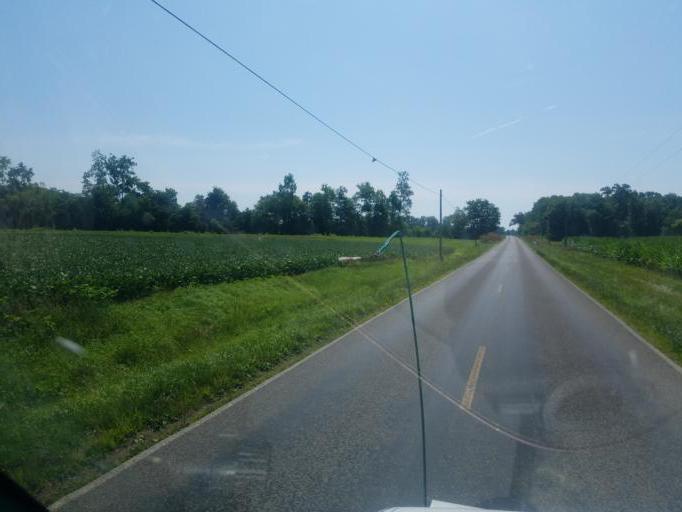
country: US
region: Ohio
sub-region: Champaign County
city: North Lewisburg
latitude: 40.2119
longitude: -83.5010
